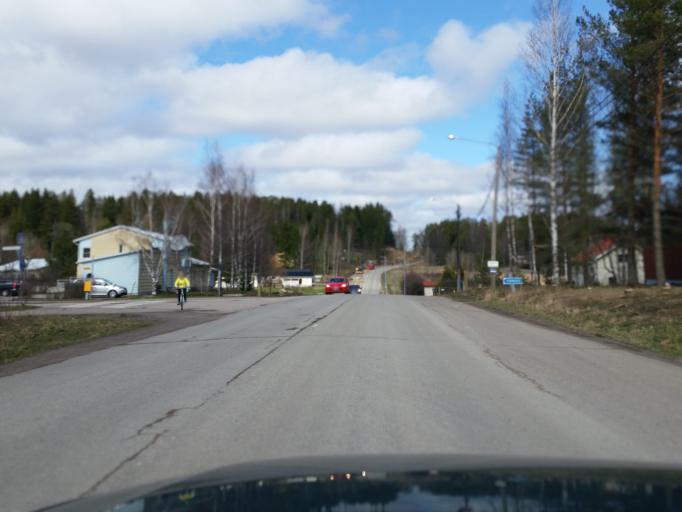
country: FI
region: Uusimaa
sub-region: Helsinki
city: Vihti
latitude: 60.4029
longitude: 24.3296
